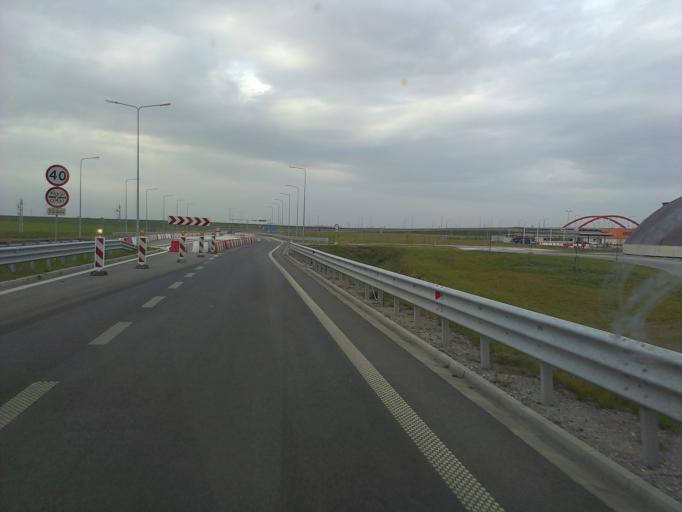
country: PL
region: Subcarpathian Voivodeship
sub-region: Powiat przemyski
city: Orly
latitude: 49.9082
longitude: 22.8156
